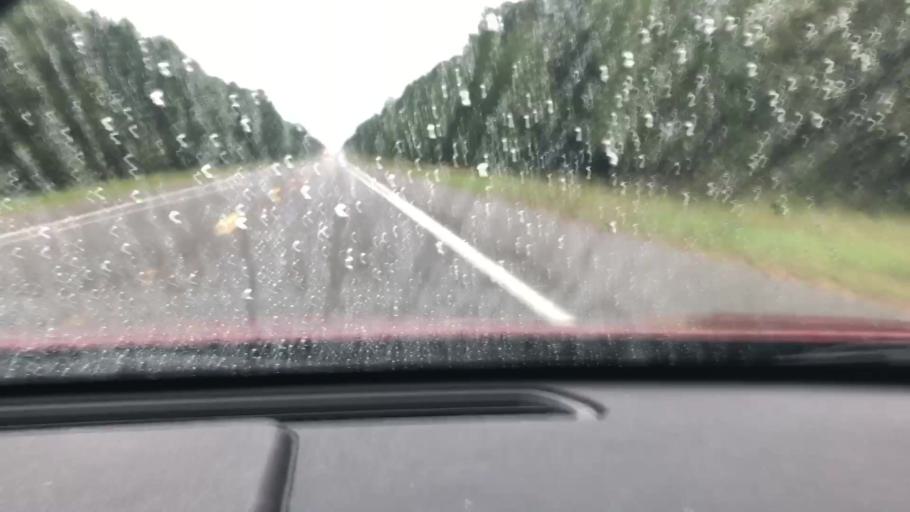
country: US
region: Arkansas
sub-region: Columbia County
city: Magnolia
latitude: 33.3040
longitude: -93.2714
